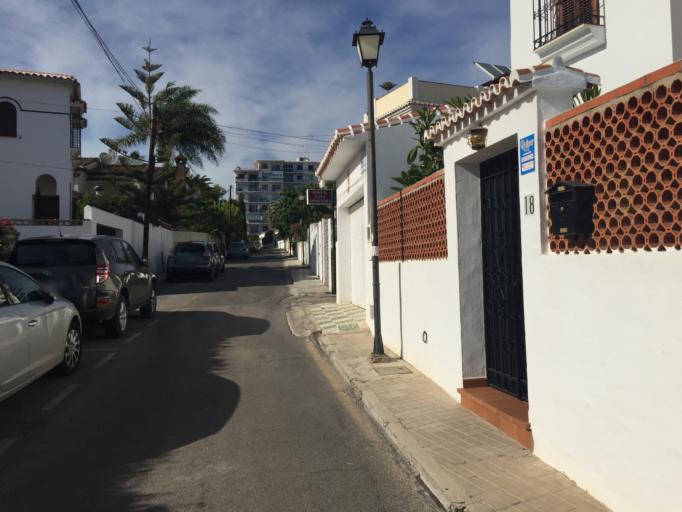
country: ES
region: Andalusia
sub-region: Provincia de Malaga
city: Nerja
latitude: 36.7537
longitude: -3.8722
